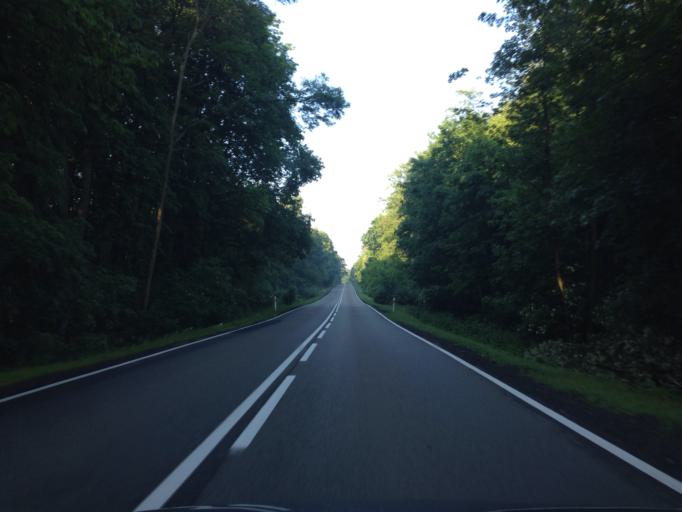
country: PL
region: Pomeranian Voivodeship
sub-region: Powiat kwidzynski
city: Gardeja
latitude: 53.5893
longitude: 18.9098
